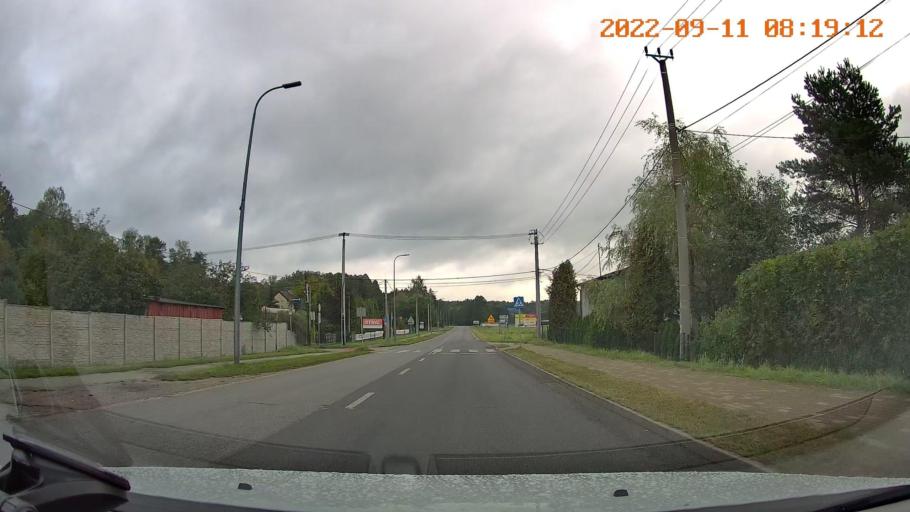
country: PL
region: Silesian Voivodeship
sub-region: Tychy
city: Tychy
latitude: 50.1500
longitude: 19.0041
